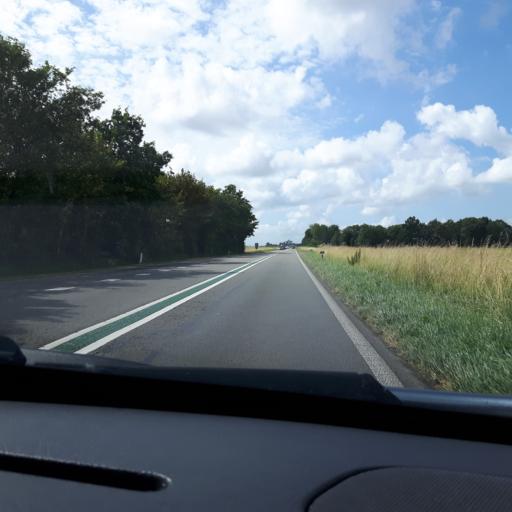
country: NL
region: Zeeland
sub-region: Gemeente Goes
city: Goes
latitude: 51.5720
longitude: 3.8350
